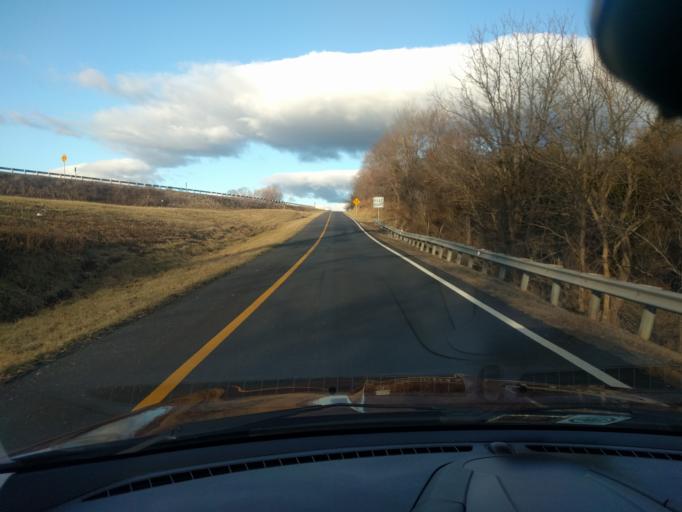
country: US
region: Virginia
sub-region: City of Bedford
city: Bedford
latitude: 37.3363
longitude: -79.5435
